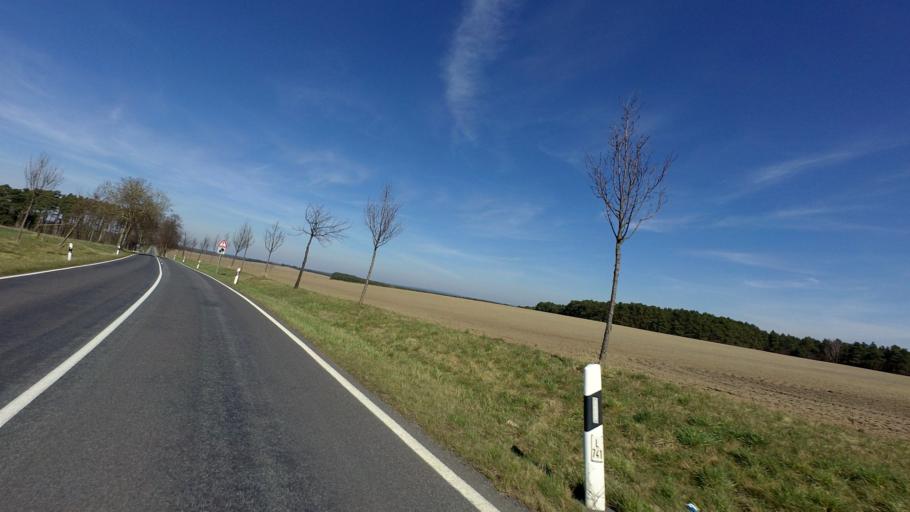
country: DE
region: Brandenburg
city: Munchehofe
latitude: 52.1699
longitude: 13.9209
